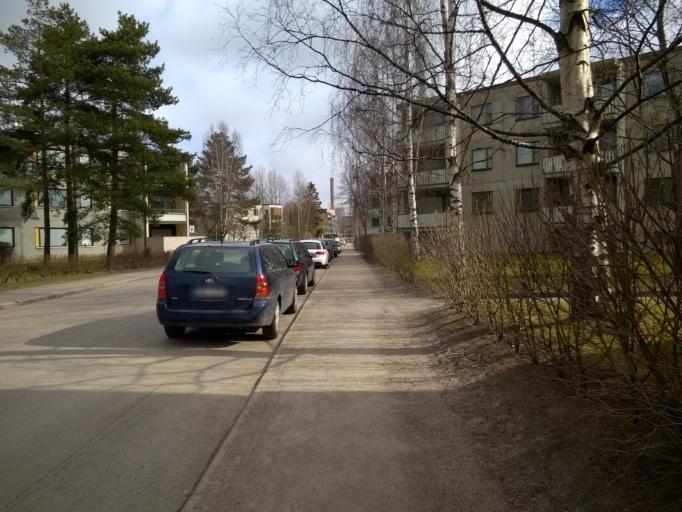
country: FI
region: Uusimaa
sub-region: Helsinki
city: Helsinki
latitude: 60.2310
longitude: 24.9698
